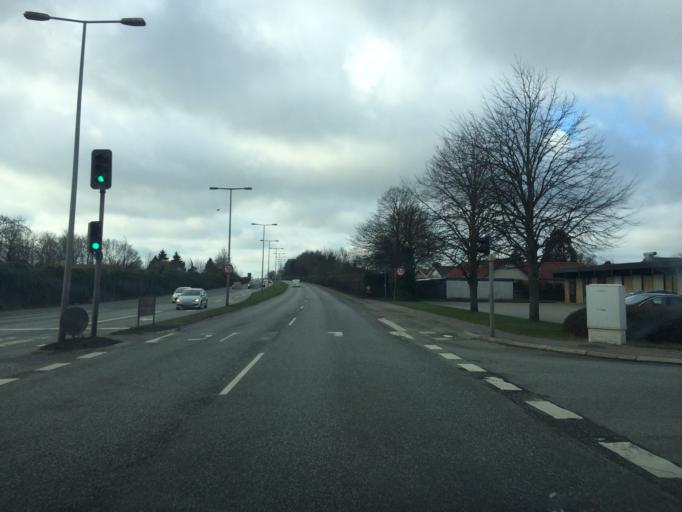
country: DK
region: South Denmark
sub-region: Fredericia Kommune
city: Snoghoj
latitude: 55.5433
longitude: 9.7194
